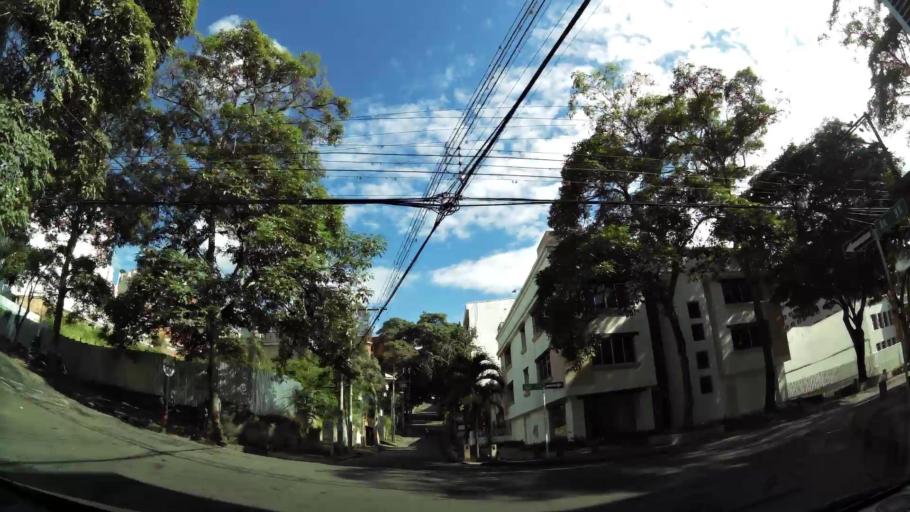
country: CO
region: Valle del Cauca
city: Cali
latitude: 3.4628
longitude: -76.5327
